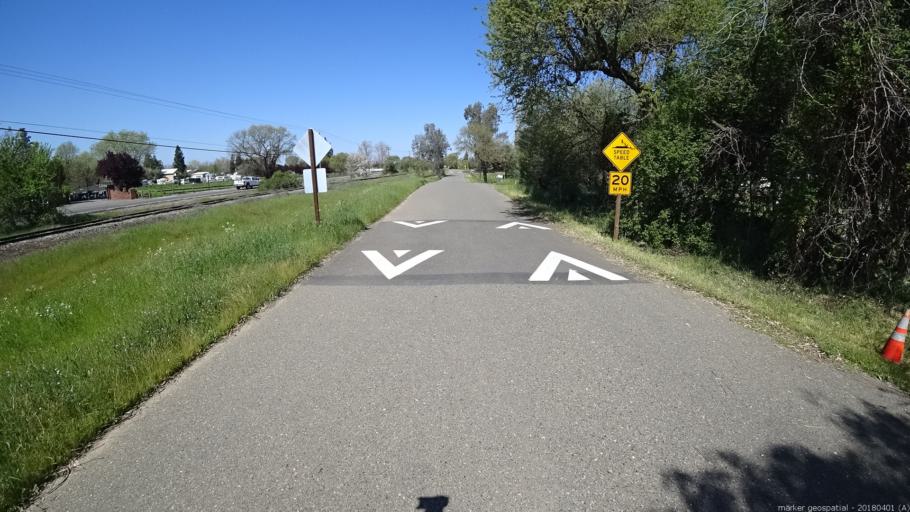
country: US
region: California
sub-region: Sacramento County
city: Wilton
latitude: 38.4128
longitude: -121.2732
